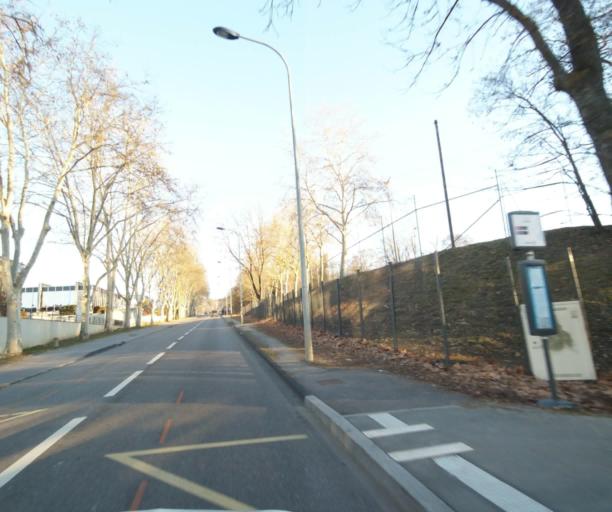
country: FR
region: Lorraine
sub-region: Departement de Meurthe-et-Moselle
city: Laxou
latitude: 48.6972
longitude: 6.1377
